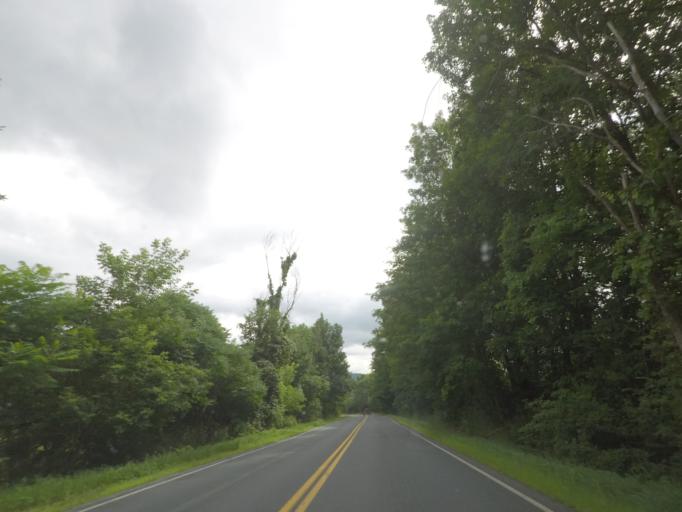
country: US
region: New York
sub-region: Saratoga County
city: Stillwater
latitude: 42.8719
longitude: -73.5597
